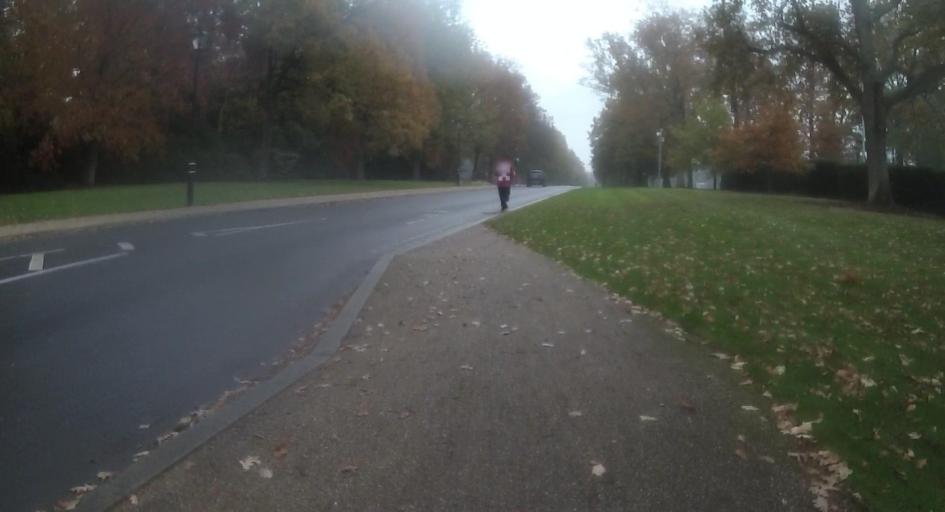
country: GB
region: England
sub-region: Bracknell Forest
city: Crowthorne
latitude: 51.3674
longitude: -0.8124
